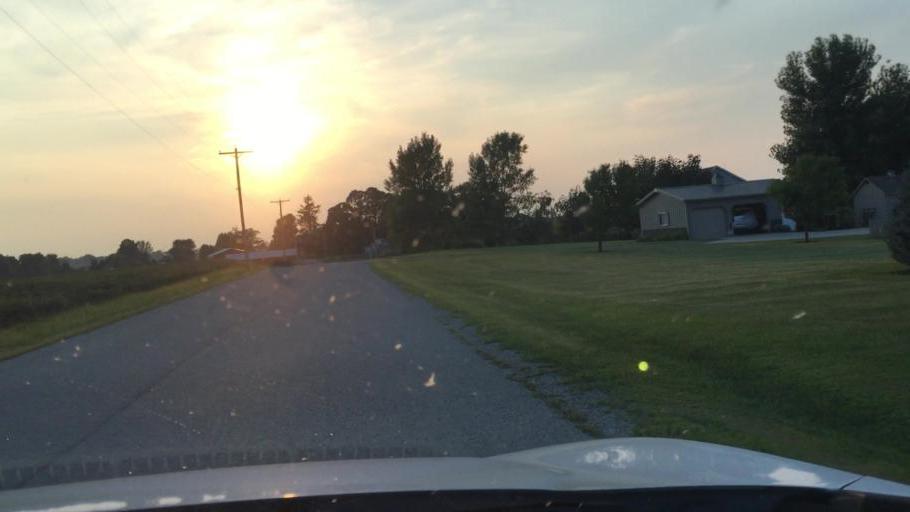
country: US
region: Ohio
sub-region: Madison County
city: Choctaw Lake
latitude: 39.9483
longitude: -83.5643
